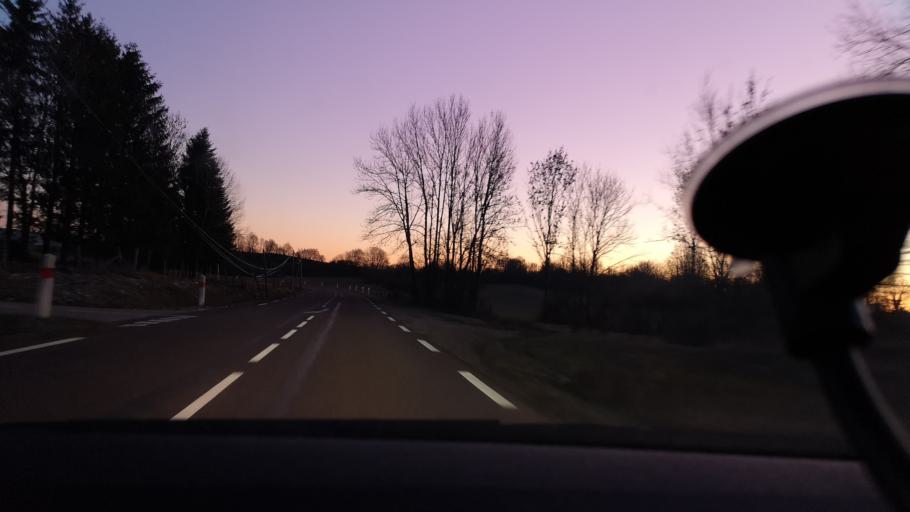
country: FR
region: Franche-Comte
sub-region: Departement du Jura
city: Champagnole
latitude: 46.7929
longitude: 6.0068
